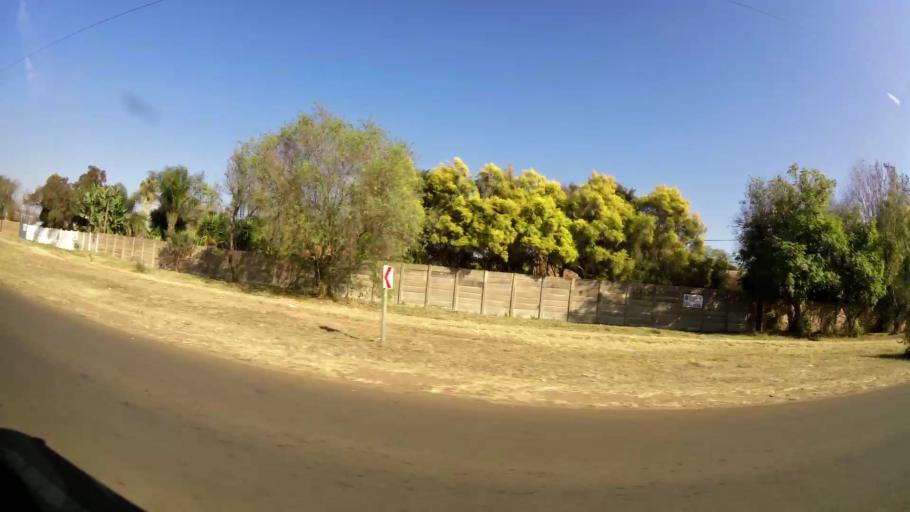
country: ZA
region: Gauteng
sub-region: City of Tshwane Metropolitan Municipality
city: Pretoria
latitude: -25.6574
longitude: 28.2442
